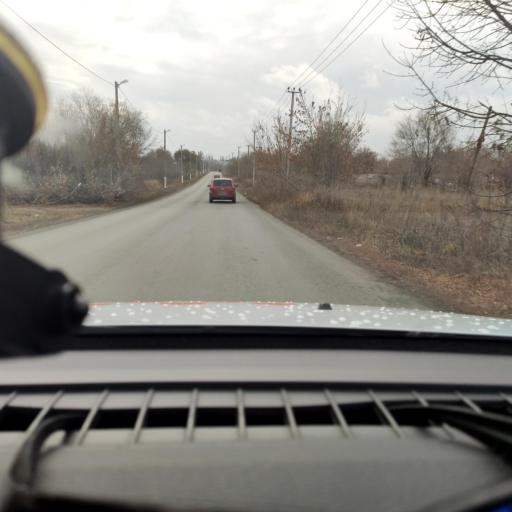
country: RU
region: Samara
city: Chapayevsk
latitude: 52.9922
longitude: 49.7306
